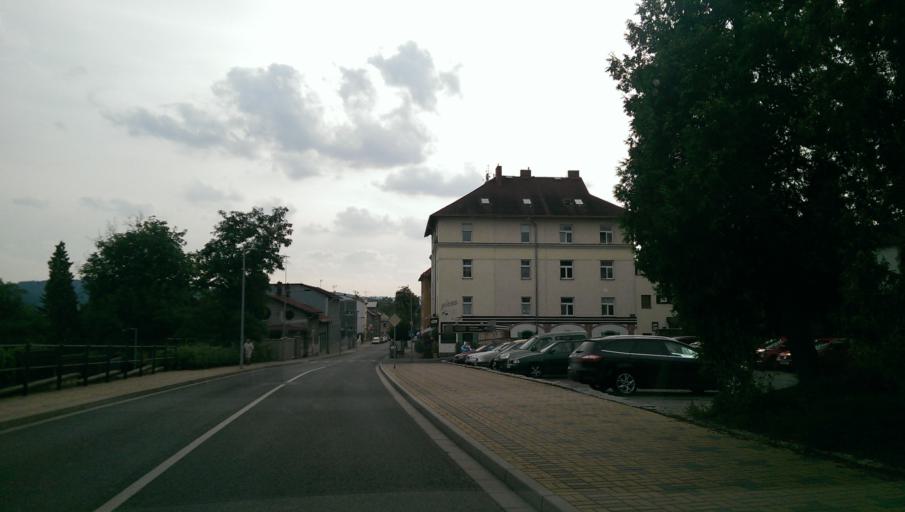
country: CZ
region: Liberecky
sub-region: Okres Semily
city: Turnov
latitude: 50.5894
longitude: 15.1487
